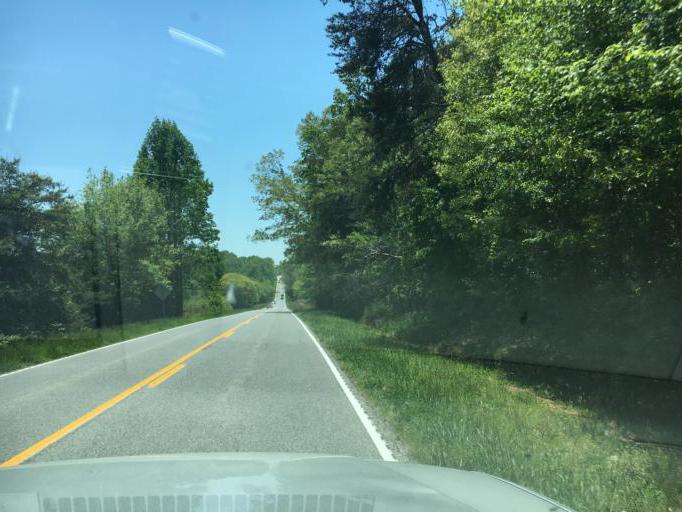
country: US
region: South Carolina
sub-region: Cherokee County
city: Blacksburg
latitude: 35.1468
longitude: -81.5745
